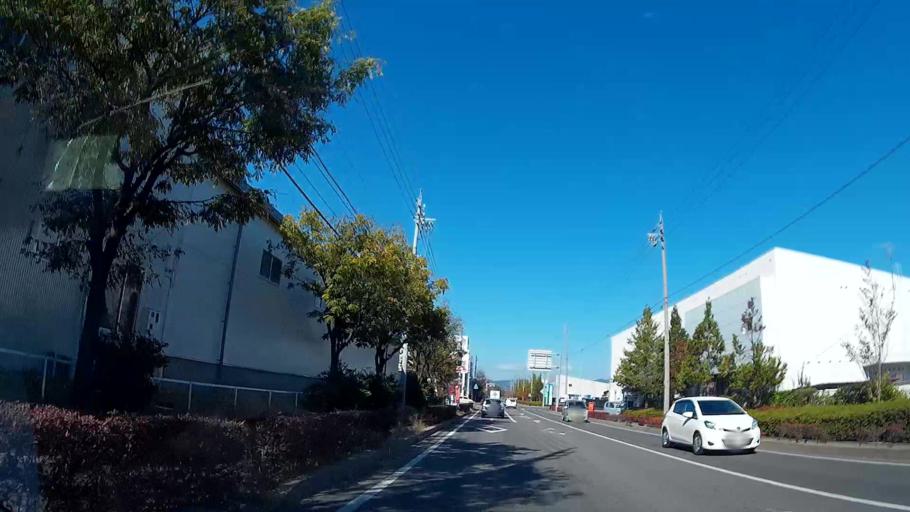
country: JP
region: Nagano
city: Matsumoto
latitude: 36.1884
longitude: 137.9491
